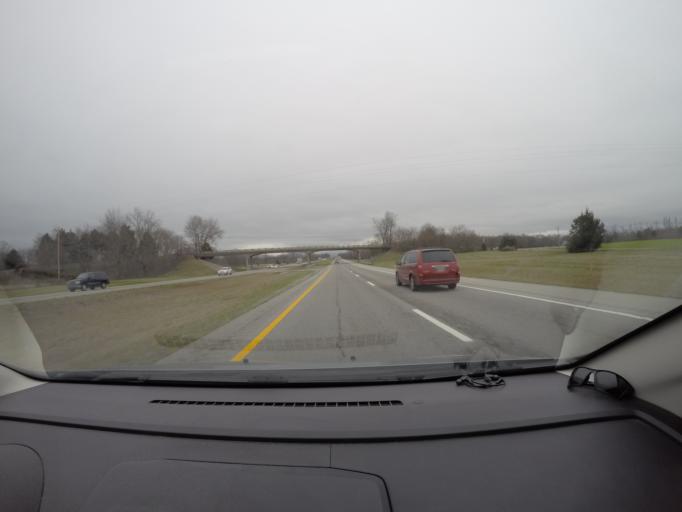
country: US
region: Tennessee
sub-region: Marion County
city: Monteagle
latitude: 35.3236
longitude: -85.9252
